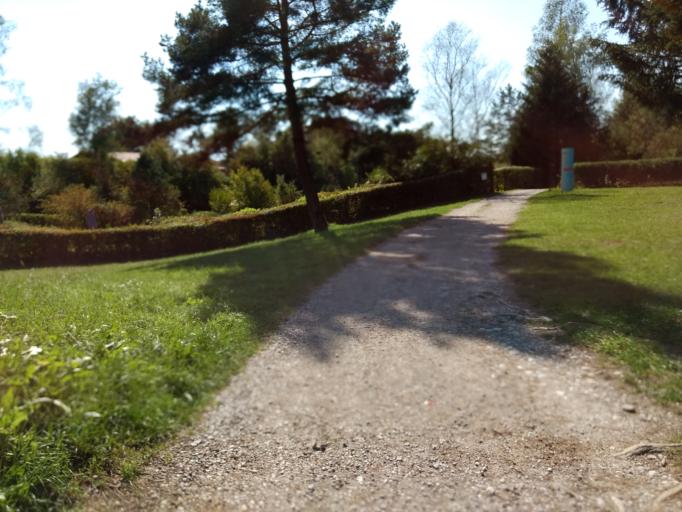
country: DE
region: Bavaria
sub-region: Upper Bavaria
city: Geretsried
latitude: 47.8371
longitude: 11.4742
